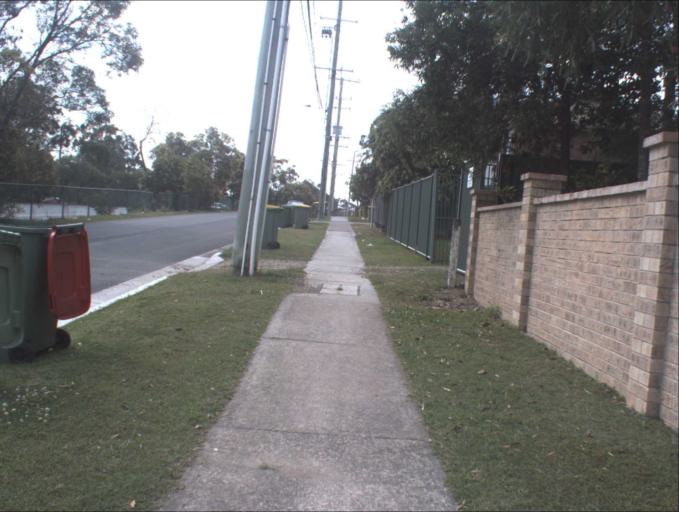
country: AU
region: Queensland
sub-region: Logan
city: Waterford West
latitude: -27.6735
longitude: 153.1223
